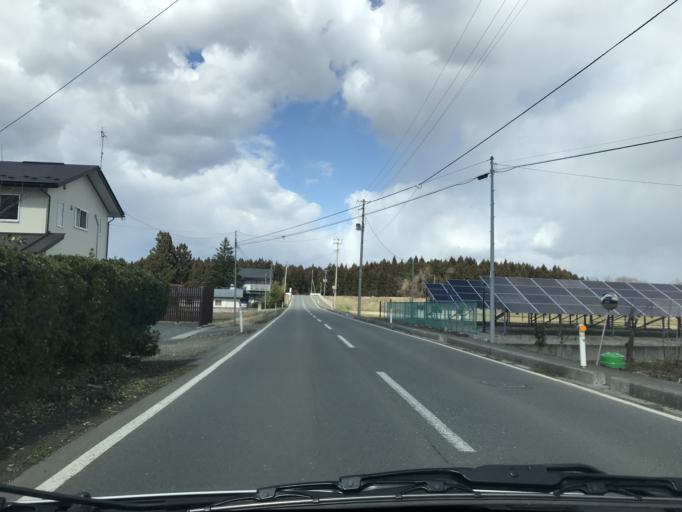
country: JP
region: Iwate
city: Kitakami
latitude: 39.2855
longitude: 141.0675
